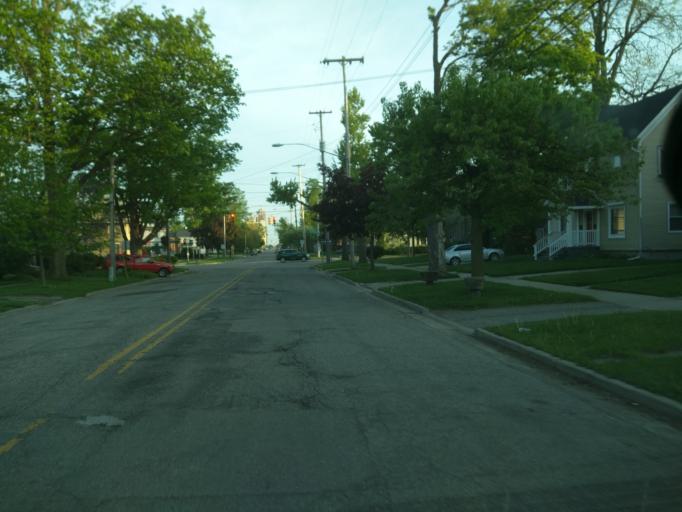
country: US
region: Michigan
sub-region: Ingham County
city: Lansing
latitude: 42.7441
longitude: -84.5538
